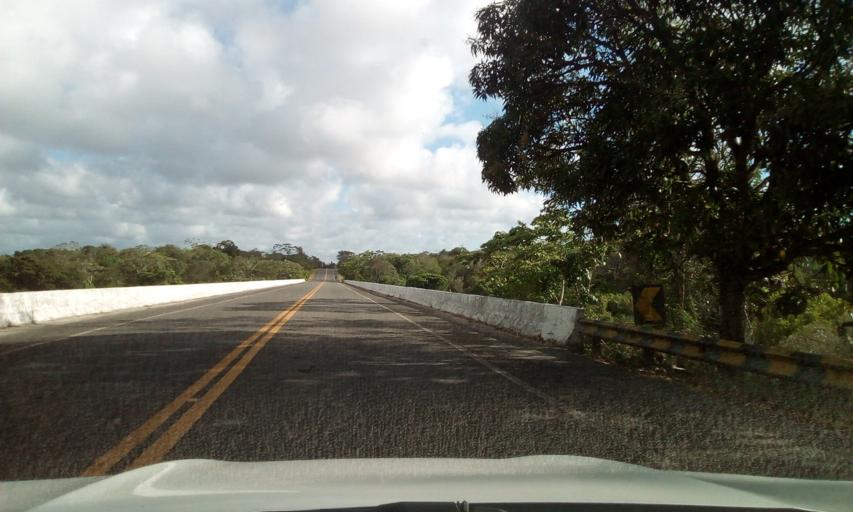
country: BR
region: Bahia
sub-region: Conde
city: Conde
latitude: -11.8077
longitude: -37.6314
